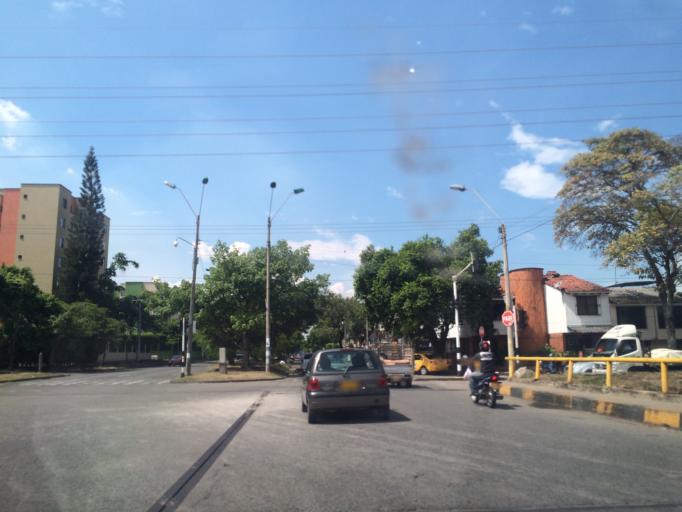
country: CO
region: Valle del Cauca
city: Cali
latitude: 3.4062
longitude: -76.5270
